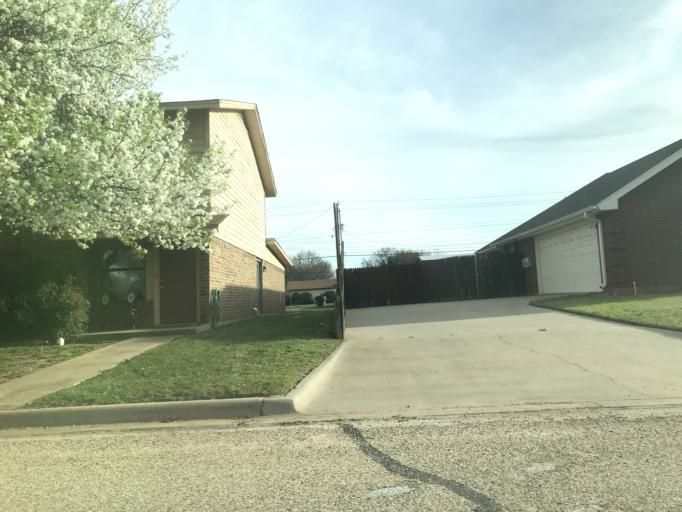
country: US
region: Texas
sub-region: Taylor County
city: Abilene
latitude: 32.3953
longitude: -99.7712
